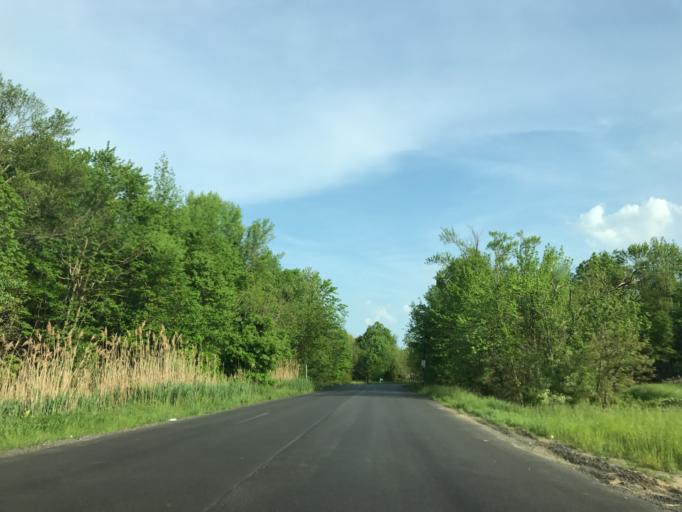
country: US
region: Maryland
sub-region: Baltimore County
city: Middle River
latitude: 39.3404
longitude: -76.4399
